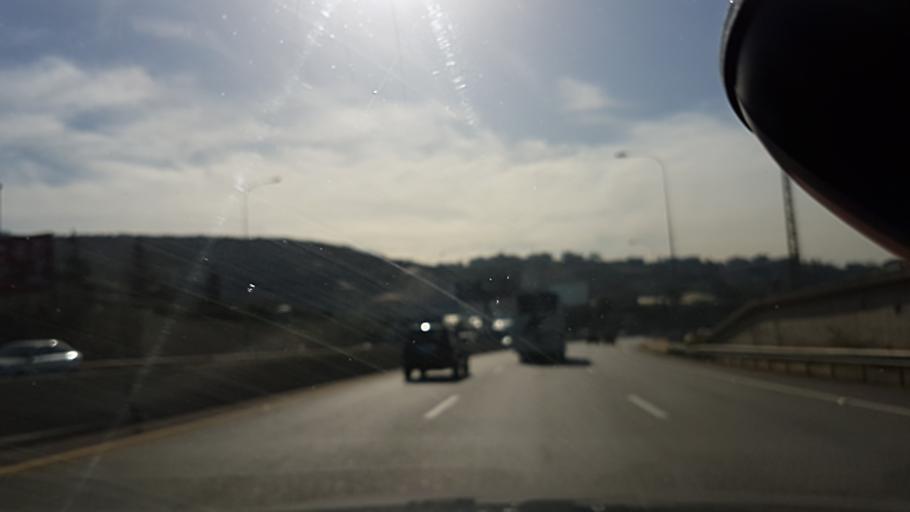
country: LB
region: Liban-Sud
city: Sidon
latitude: 33.6134
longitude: 35.4054
